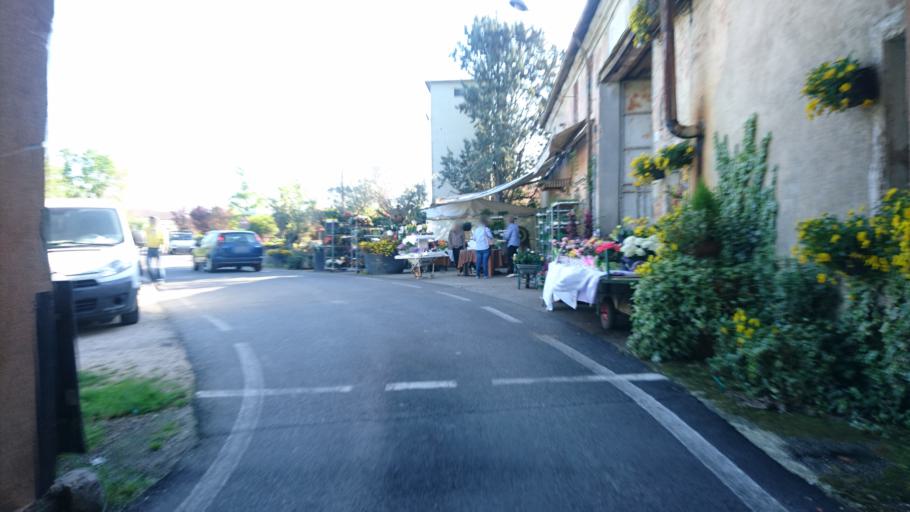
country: IT
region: Veneto
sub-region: Provincia di Padova
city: Massanzago-Ca' Baglioni-San Dono
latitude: 45.5487
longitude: 11.9995
